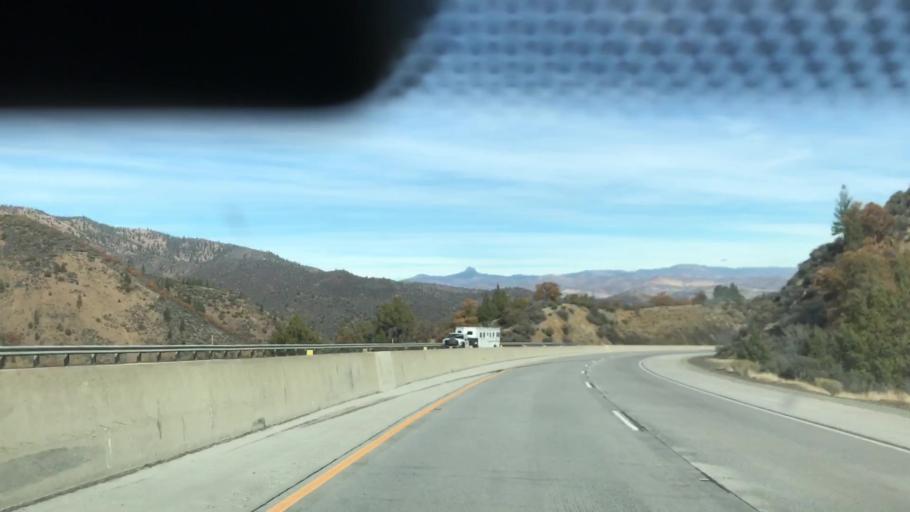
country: US
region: California
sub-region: Siskiyou County
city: Yreka
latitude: 41.8311
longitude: -122.5802
